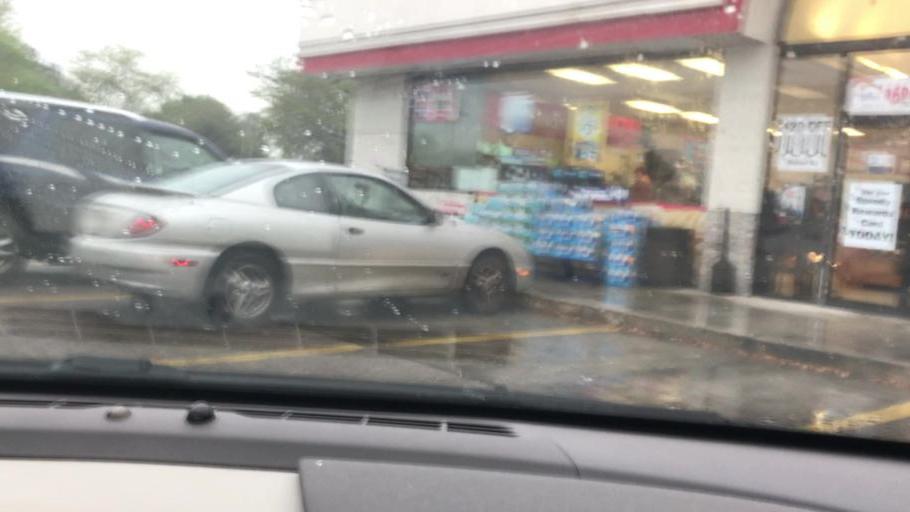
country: US
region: Florida
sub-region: Lee County
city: Palmona Park
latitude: 26.7246
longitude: -81.9071
